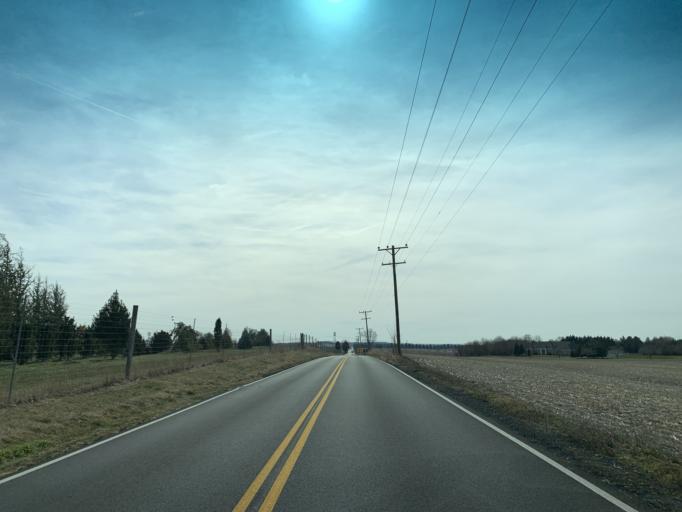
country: US
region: Maryland
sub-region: Frederick County
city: Adamstown
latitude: 39.2988
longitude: -77.4650
